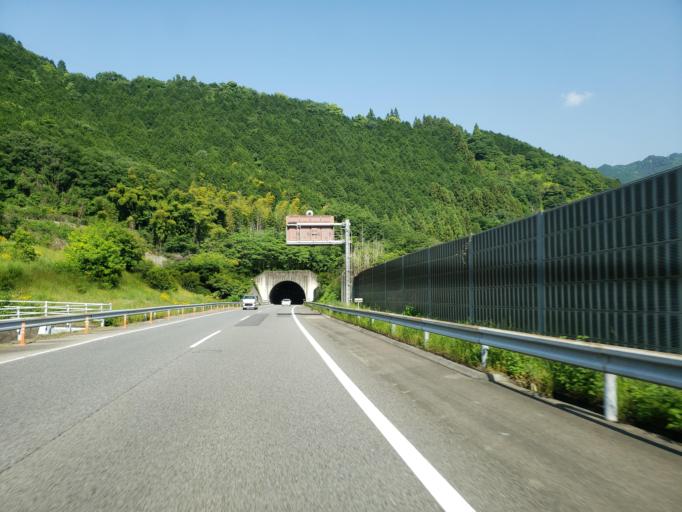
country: JP
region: Ehime
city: Saijo
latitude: 33.8866
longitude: 133.1731
